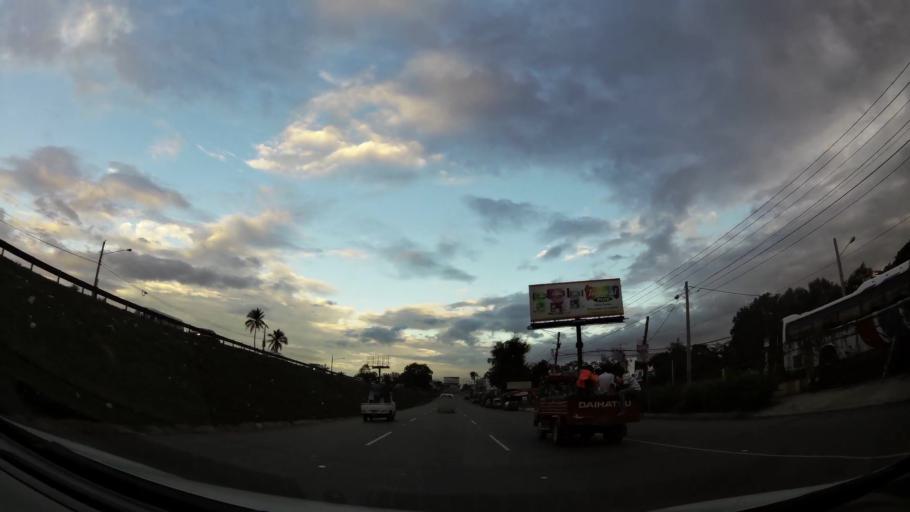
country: DO
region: Santo Domingo
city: Santo Domingo Oeste
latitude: 18.5371
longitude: -70.0201
